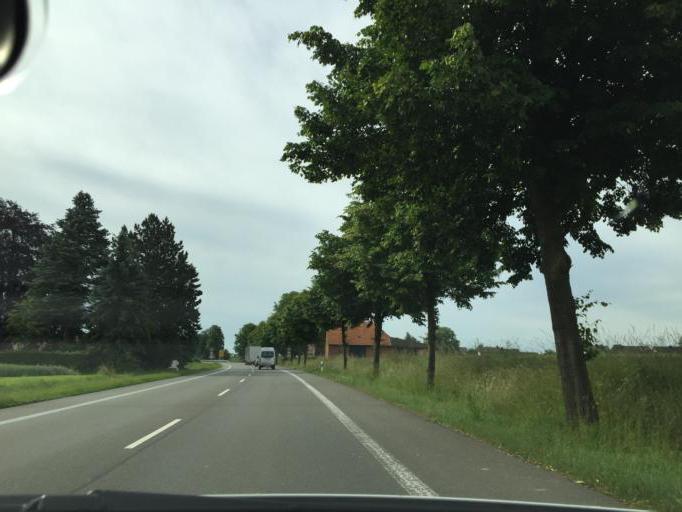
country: DE
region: North Rhine-Westphalia
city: Warburg
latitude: 51.5382
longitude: 9.1343
